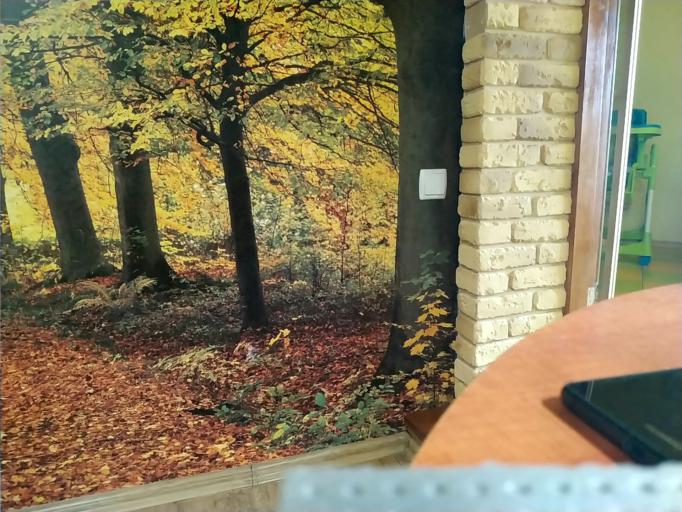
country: RU
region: Tverskaya
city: Kalashnikovo
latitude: 57.2641
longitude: 35.1402
